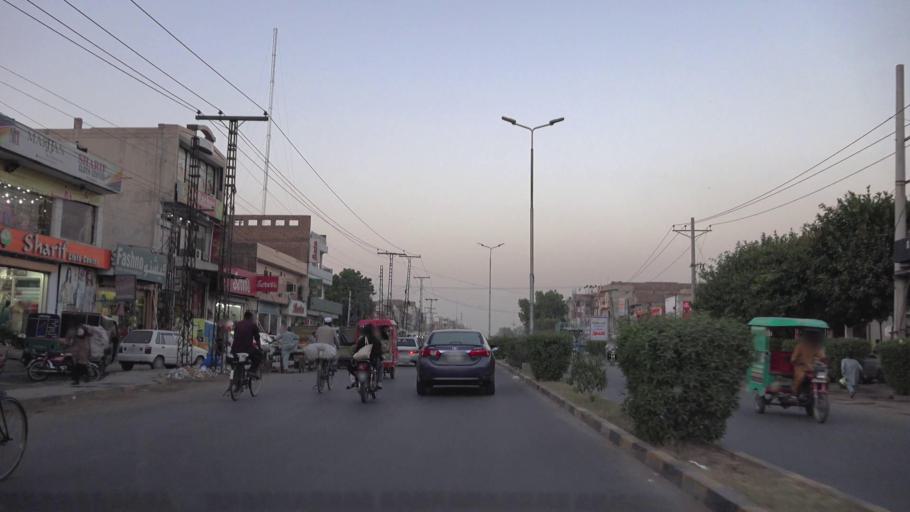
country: PK
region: Punjab
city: Faisalabad
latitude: 31.4486
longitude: 73.0972
